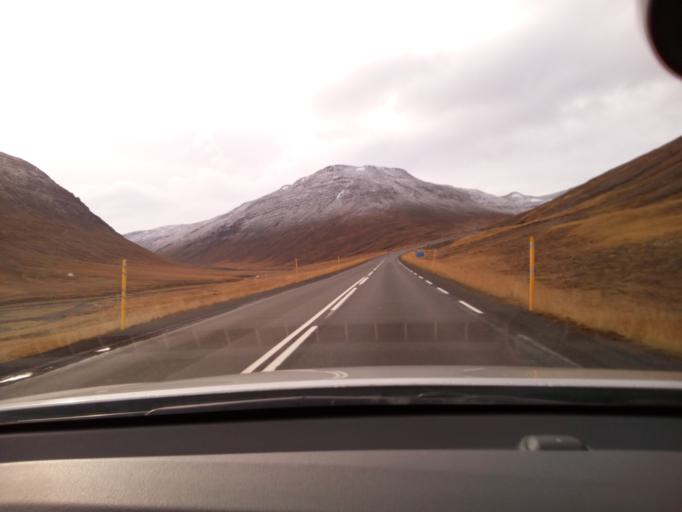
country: IS
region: Northeast
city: Dalvik
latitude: 65.4840
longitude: -18.6507
